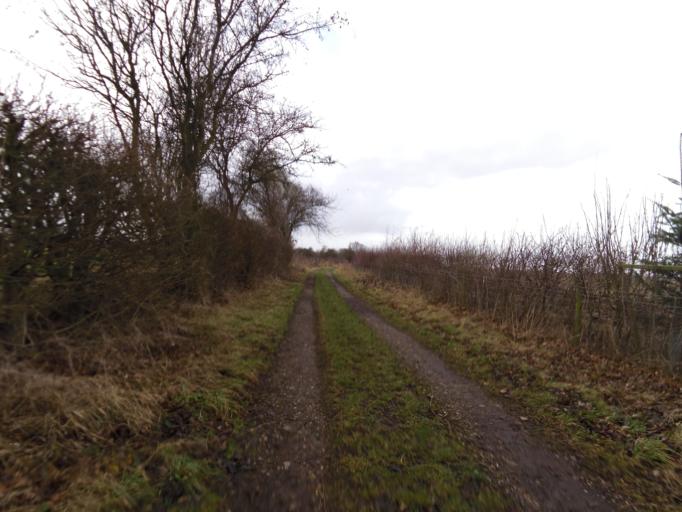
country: GB
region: England
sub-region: Suffolk
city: Needham Market
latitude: 52.1569
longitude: 1.0698
